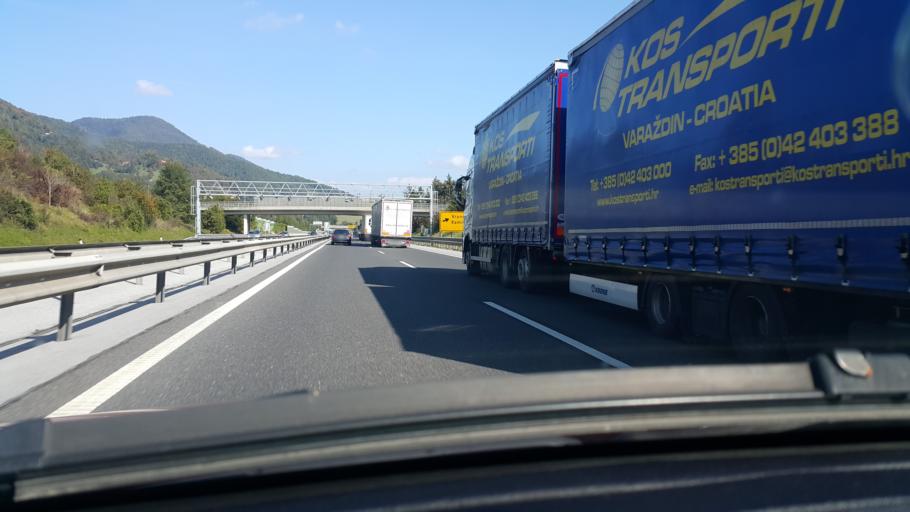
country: SI
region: Vransko
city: Vransko
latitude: 46.2447
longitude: 14.9646
